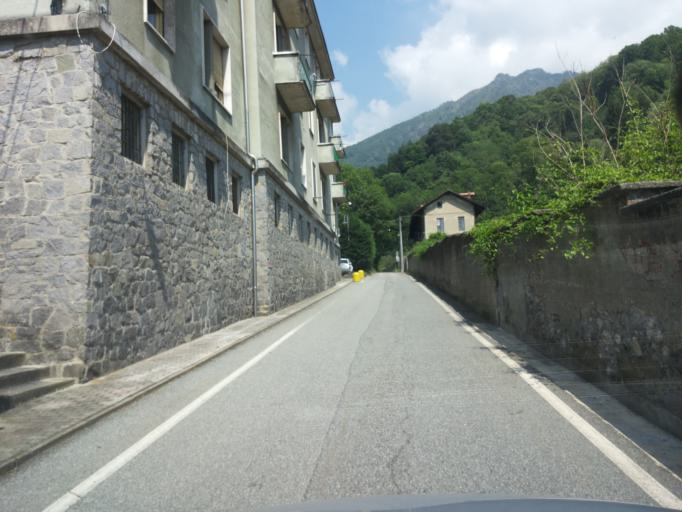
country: IT
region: Piedmont
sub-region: Provincia di Biella
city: Coggiola
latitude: 45.6926
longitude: 8.1704
